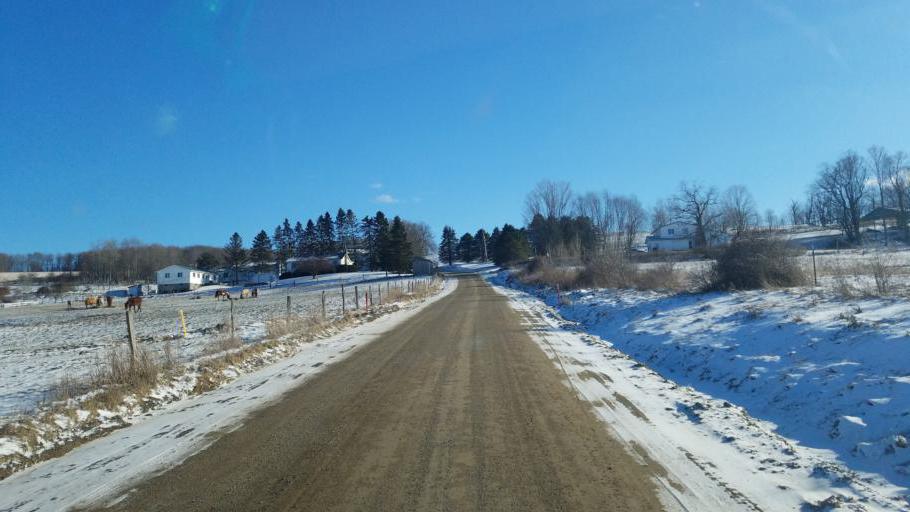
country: US
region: New York
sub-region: Allegany County
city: Andover
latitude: 41.9486
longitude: -77.7699
